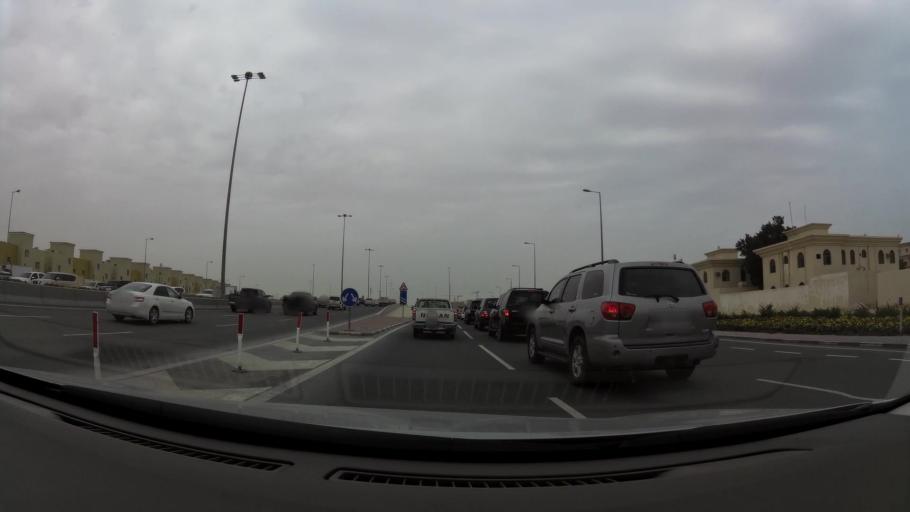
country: QA
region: Baladiyat ar Rayyan
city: Ar Rayyan
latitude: 25.3419
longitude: 51.4594
